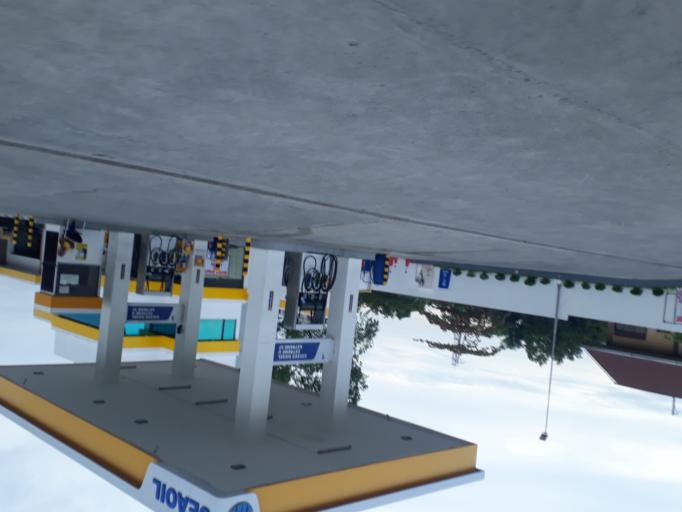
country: PH
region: Central Luzon
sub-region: Province of Bulacan
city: Obando
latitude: 14.7014
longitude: 120.9501
